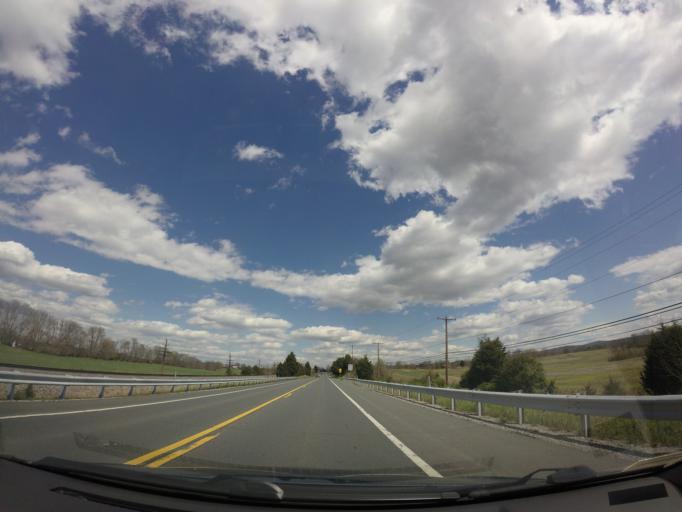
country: US
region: West Virginia
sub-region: Jefferson County
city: Shepherdstown
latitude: 39.4473
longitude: -77.7733
